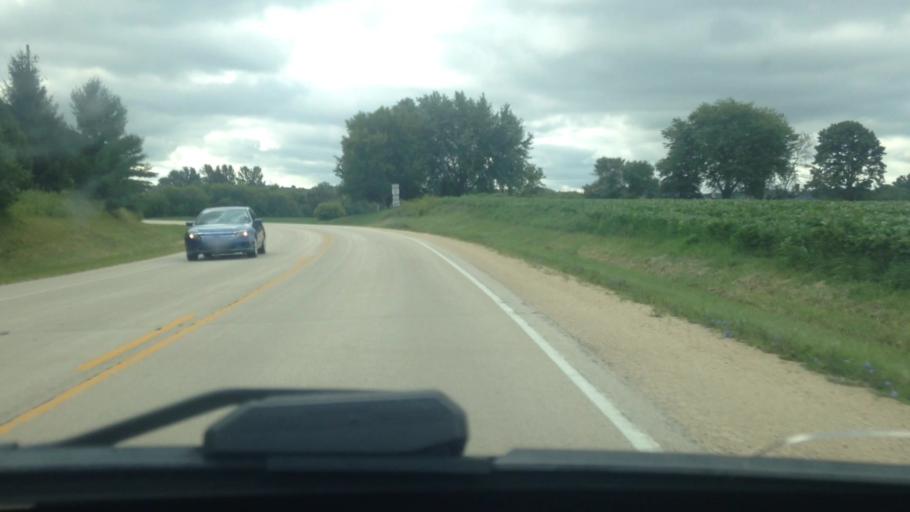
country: US
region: Wisconsin
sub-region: Dodge County
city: Mayville
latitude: 43.4799
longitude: -88.5062
